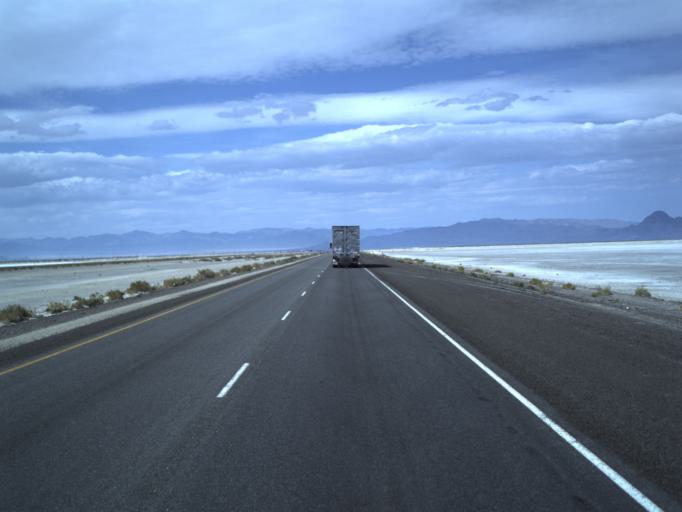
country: US
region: Utah
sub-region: Tooele County
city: Wendover
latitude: 40.7379
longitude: -113.7795
